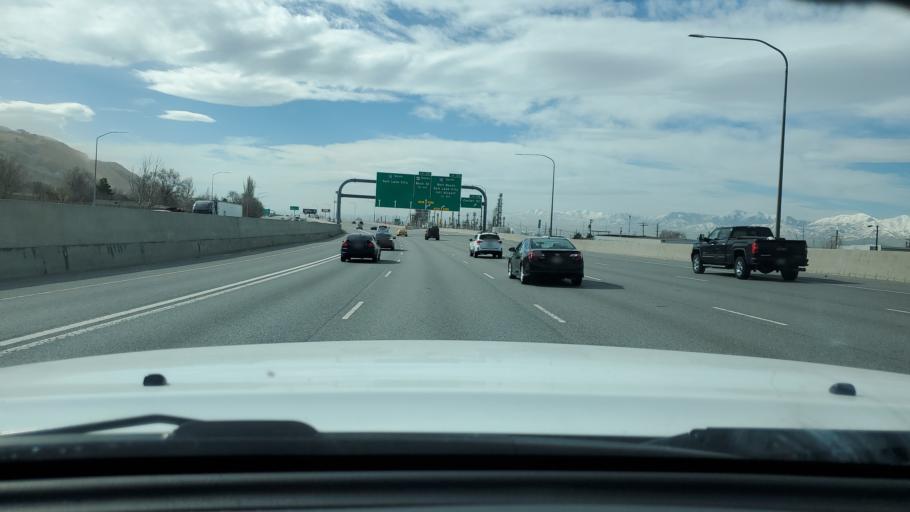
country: US
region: Utah
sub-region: Davis County
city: North Salt Lake
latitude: 40.8473
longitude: -111.9149
